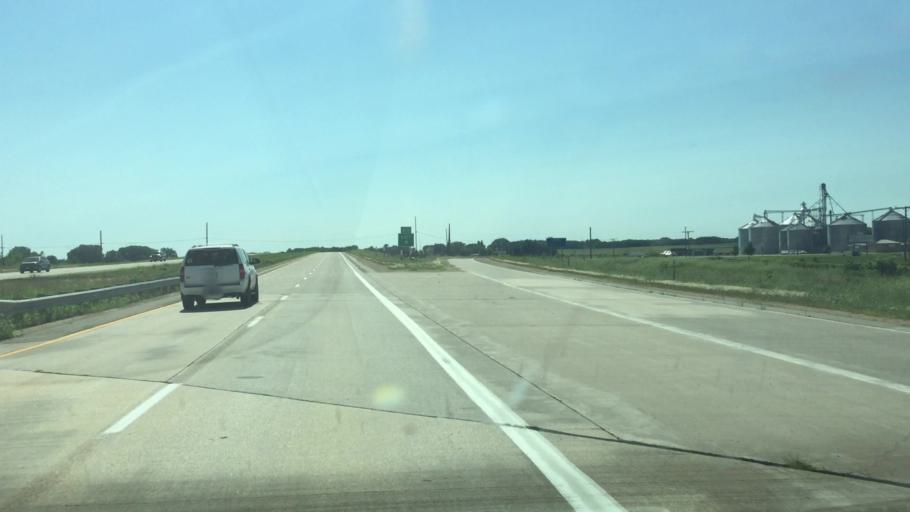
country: US
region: Iowa
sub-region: Jones County
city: Monticello
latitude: 42.2082
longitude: -91.1824
